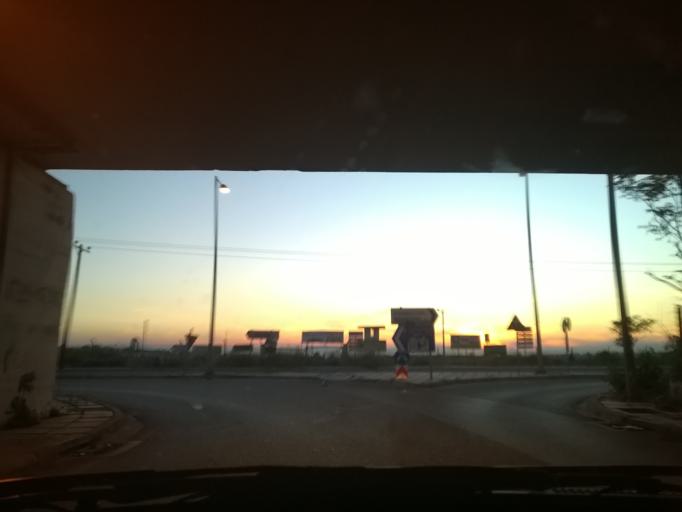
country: GR
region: Central Macedonia
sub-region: Nomos Thessalonikis
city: Polichni
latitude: 40.6743
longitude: 22.9603
